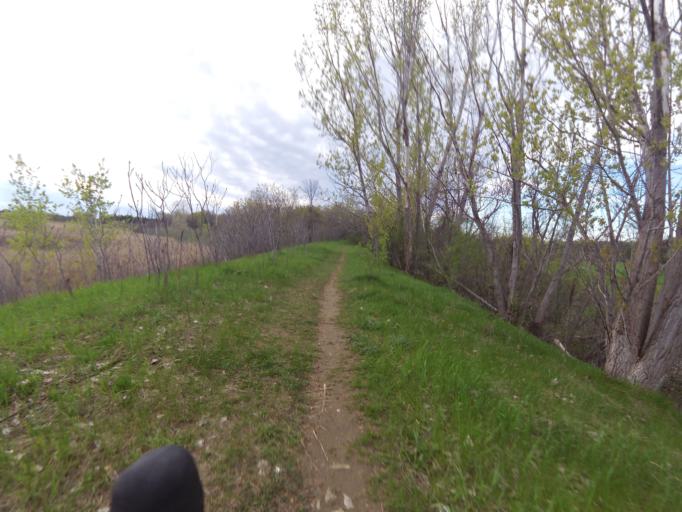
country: CA
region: Ontario
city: Bells Corners
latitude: 45.2738
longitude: -75.7953
